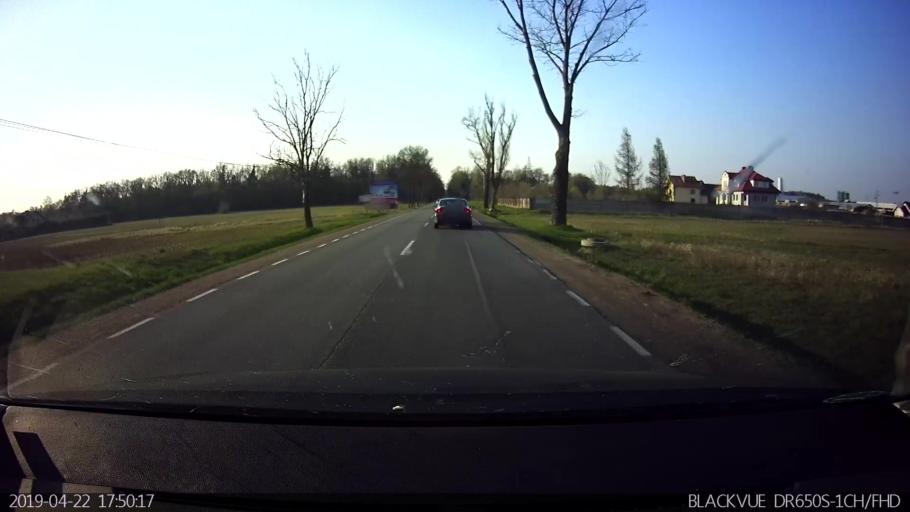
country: PL
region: Masovian Voivodeship
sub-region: Powiat wegrowski
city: Wegrow
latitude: 52.4228
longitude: 22.0030
